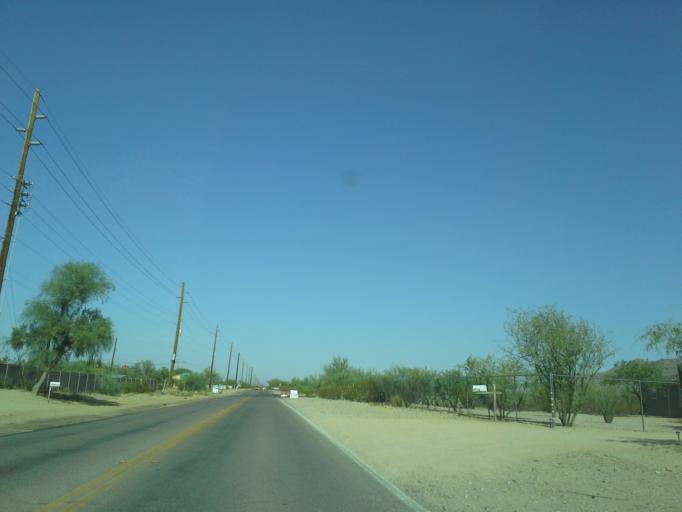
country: US
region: Arizona
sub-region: Maricopa County
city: Queen Creek
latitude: 33.2047
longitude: -111.6704
